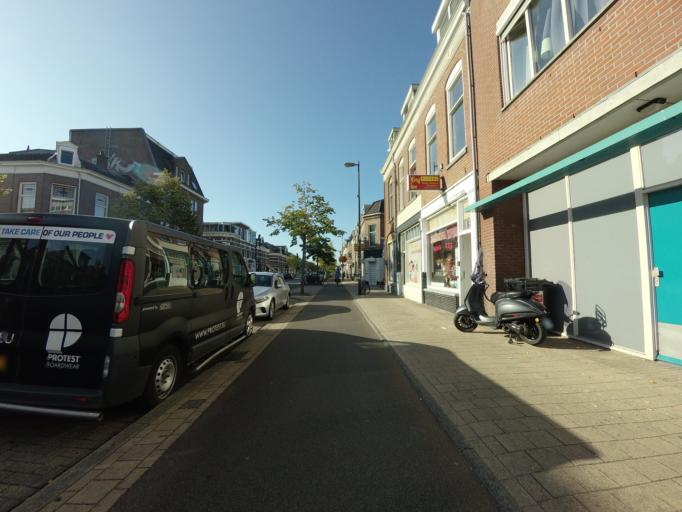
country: NL
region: Utrecht
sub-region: Gemeente Utrecht
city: Utrecht
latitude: 52.0991
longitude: 5.1030
